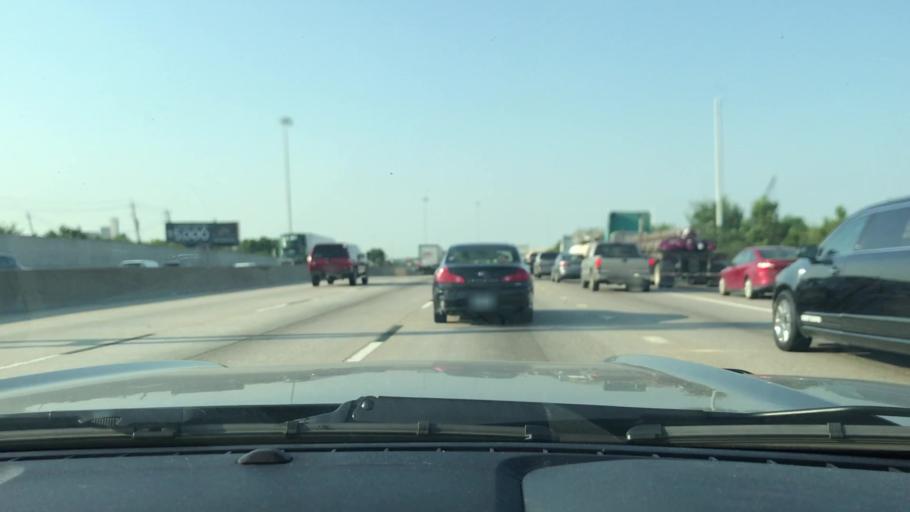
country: US
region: Texas
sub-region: Harris County
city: Jacinto City
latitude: 29.7647
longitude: -95.2653
